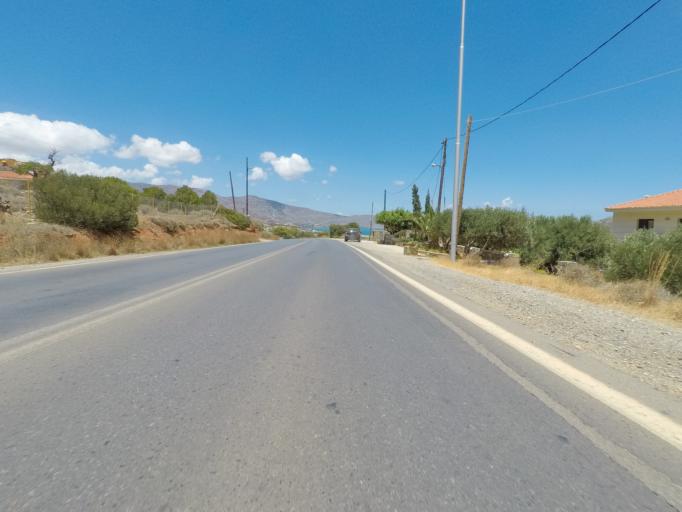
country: GR
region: Crete
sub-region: Nomos Lasithiou
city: Skhisma
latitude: 35.2437
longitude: 25.7258
